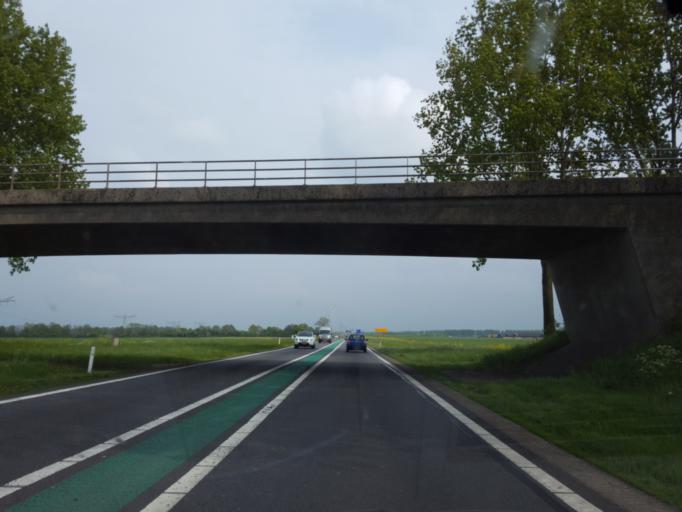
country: NL
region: Gelderland
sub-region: Gemeente Wijchen
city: Bergharen
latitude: 51.8653
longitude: 5.6904
